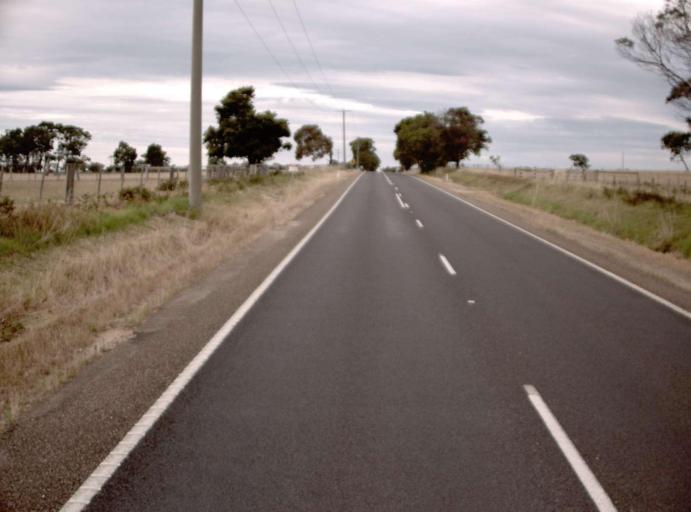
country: AU
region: Victoria
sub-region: East Gippsland
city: Bairnsdale
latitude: -37.9037
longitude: 147.6938
